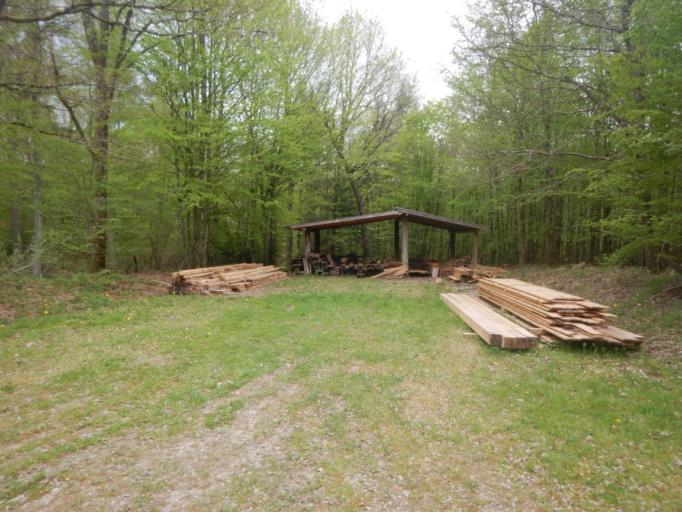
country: LU
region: Grevenmacher
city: Gonderange
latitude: 49.6861
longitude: 6.2711
